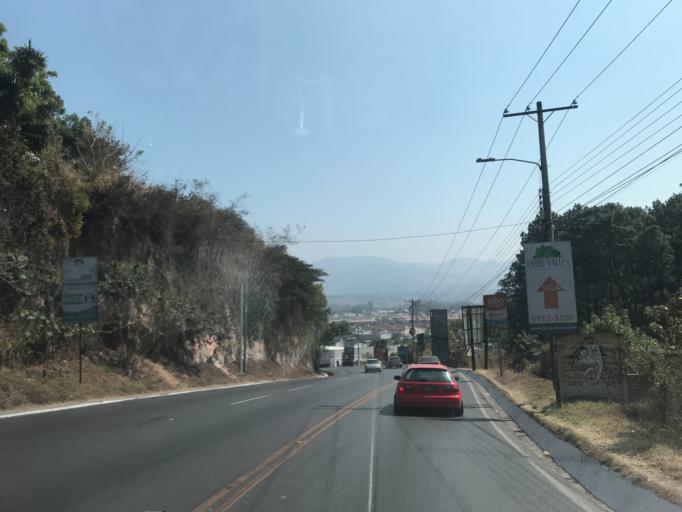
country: GT
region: Guatemala
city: Petapa
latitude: 14.5127
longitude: -90.5671
